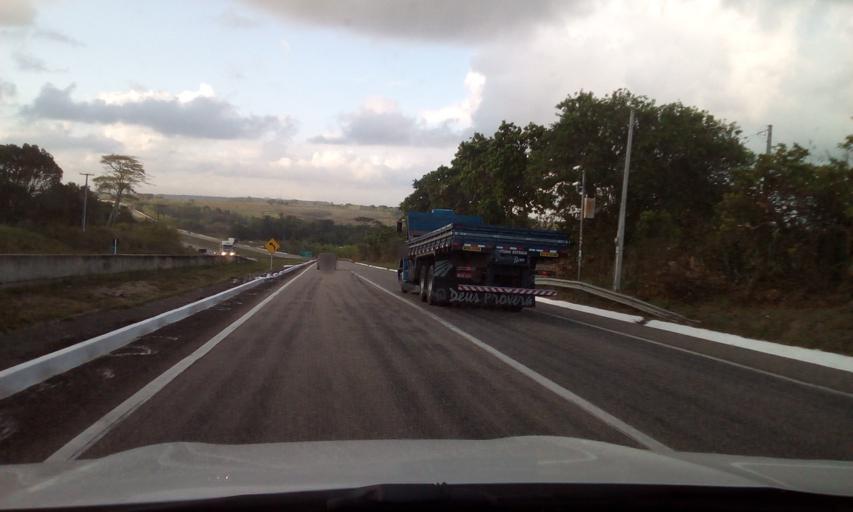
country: BR
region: Paraiba
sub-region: Alhandra
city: Alhandra
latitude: -7.3782
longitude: -34.9566
